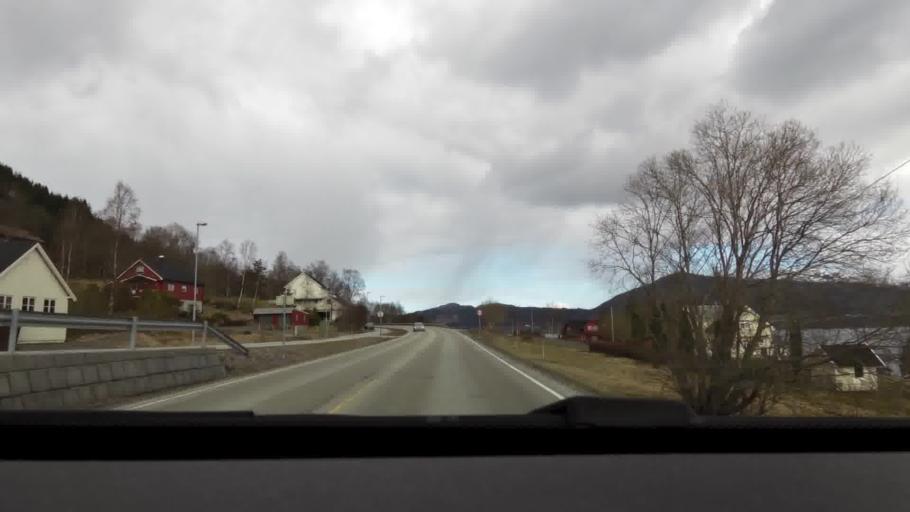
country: NO
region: More og Romsdal
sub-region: Eide
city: Eide
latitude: 62.9260
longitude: 7.4472
